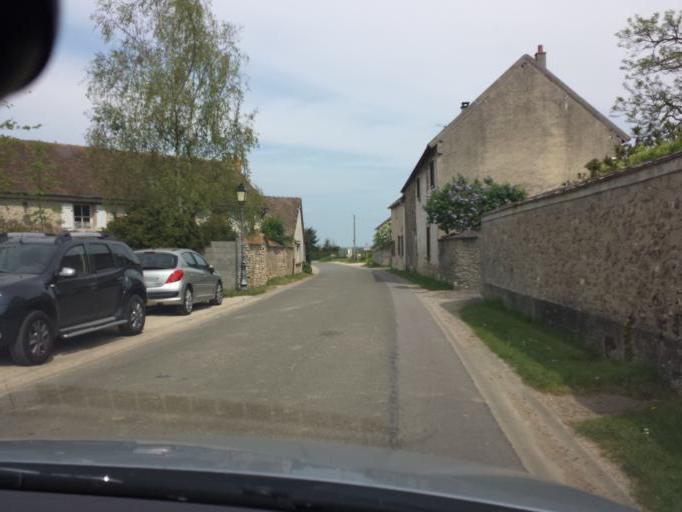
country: FR
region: Ile-de-France
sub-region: Departement des Yvelines
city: Longnes
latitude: 48.8601
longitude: 1.5891
